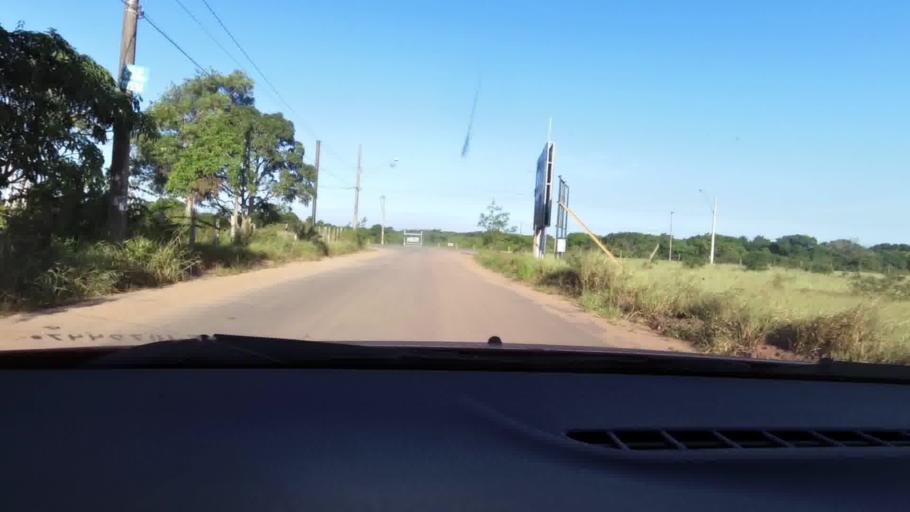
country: BR
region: Espirito Santo
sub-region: Guarapari
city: Guarapari
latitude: -20.5560
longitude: -40.4043
